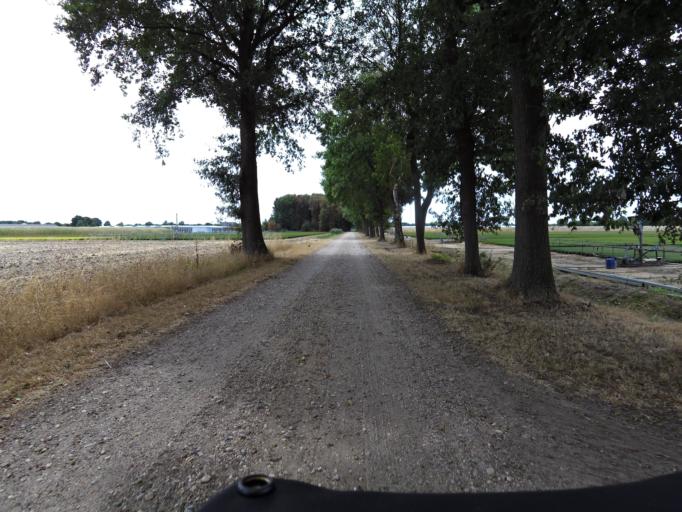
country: DE
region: North Rhine-Westphalia
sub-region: Regierungsbezirk Dusseldorf
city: Kevelaer
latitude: 51.5559
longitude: 6.2343
